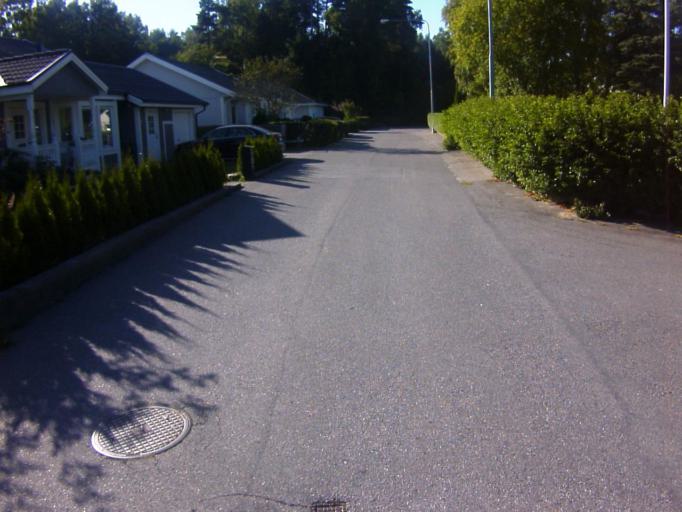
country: SE
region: Soedermanland
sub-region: Eskilstuna Kommun
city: Hallbybrunn
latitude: 59.3913
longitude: 16.4091
